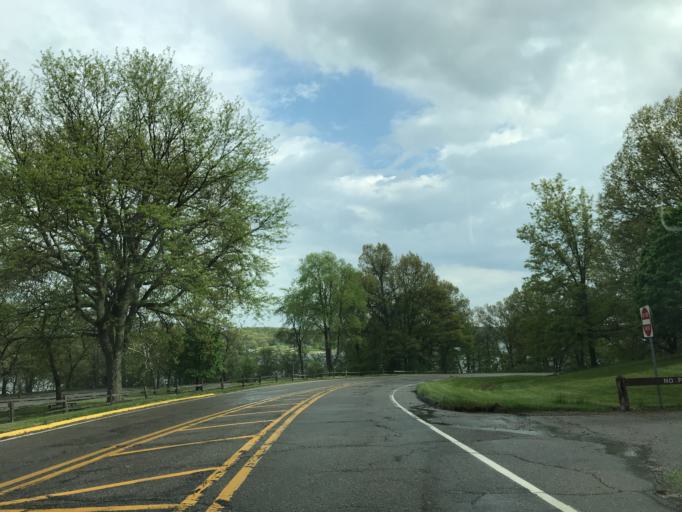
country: US
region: Michigan
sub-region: Oakland County
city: Milford
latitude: 42.5368
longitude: -83.6423
